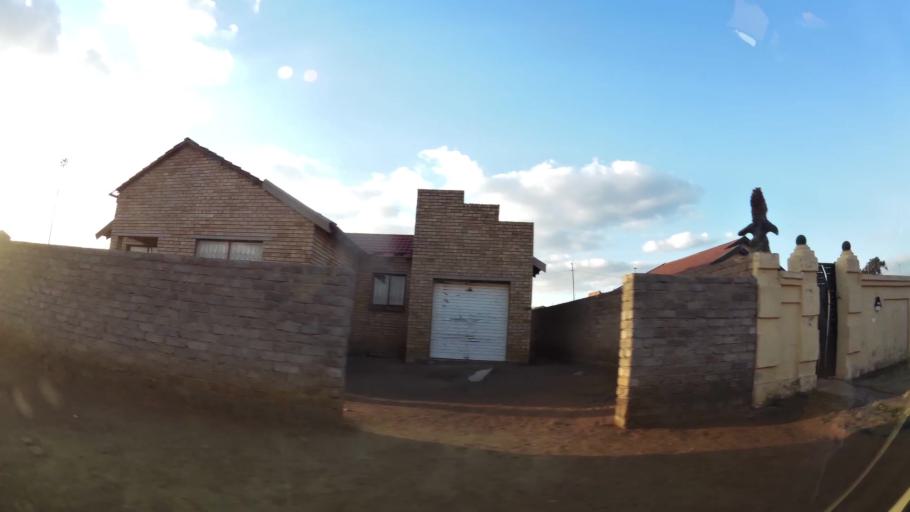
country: ZA
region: Gauteng
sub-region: West Rand District Municipality
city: Krugersdorp
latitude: -26.0768
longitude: 27.7546
